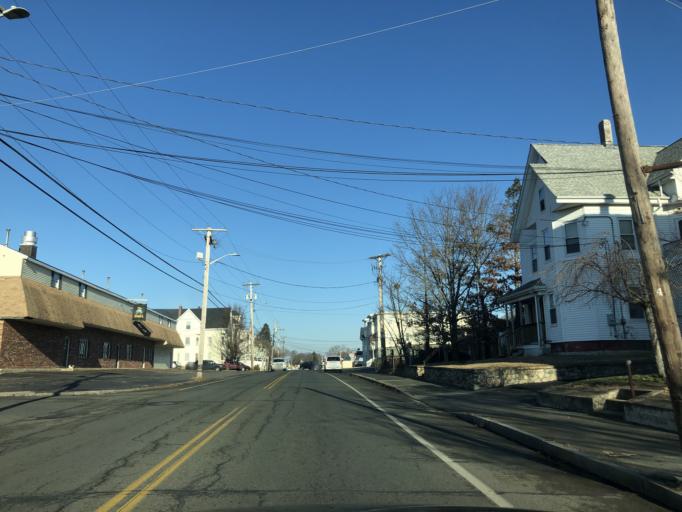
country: US
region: Massachusetts
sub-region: Plymouth County
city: Brockton
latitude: 42.1041
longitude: -71.0210
